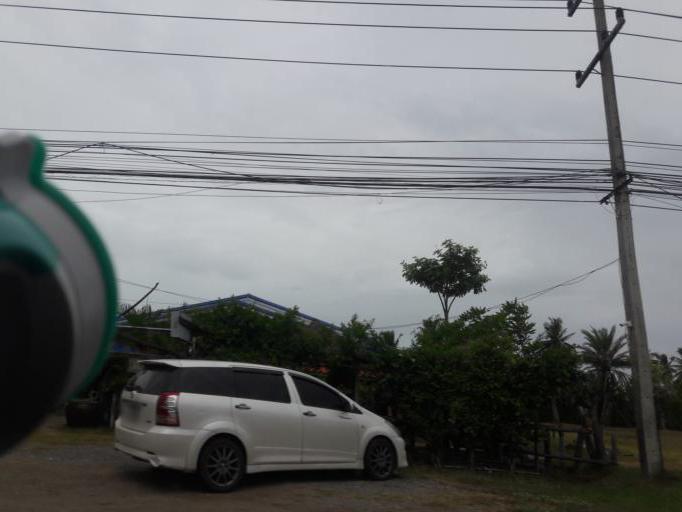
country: TH
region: Ratchaburi
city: Damnoen Saduak
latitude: 13.5477
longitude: 99.9666
